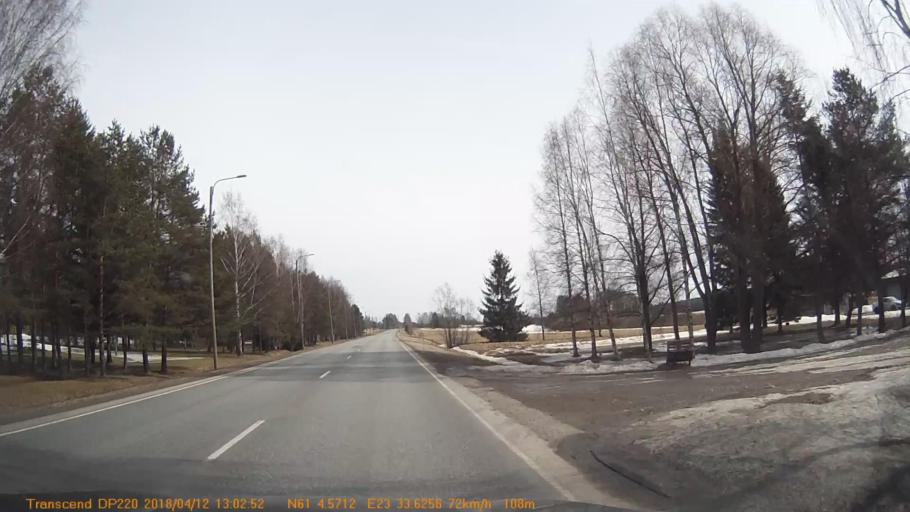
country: FI
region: Pirkanmaa
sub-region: Etelae-Pirkanmaa
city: Urjala
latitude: 61.0760
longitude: 23.5614
